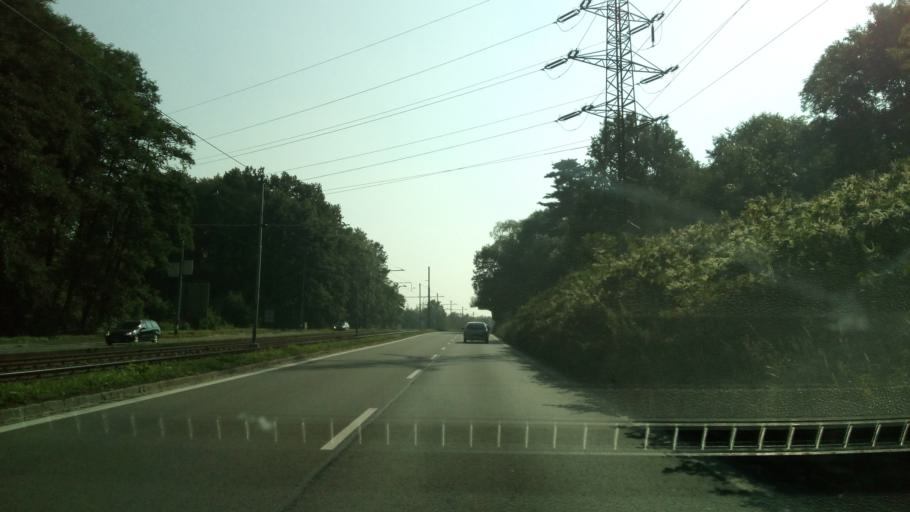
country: CZ
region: Moravskoslezsky
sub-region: Okres Ostrava-Mesto
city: Ostrava
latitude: 49.8219
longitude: 18.2356
